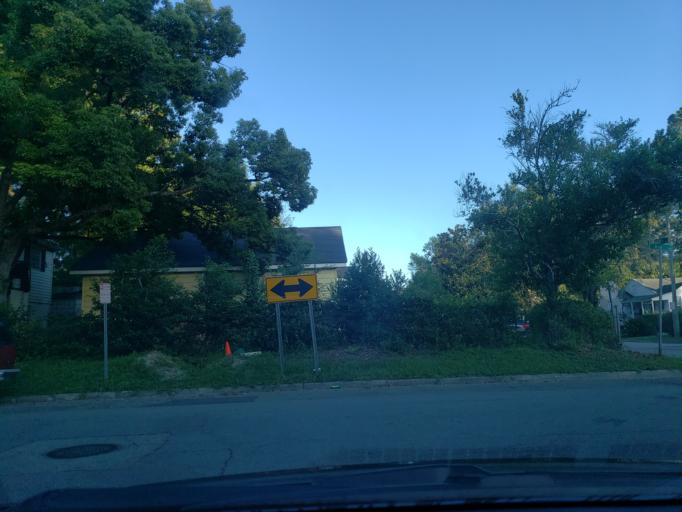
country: US
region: Georgia
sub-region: Chatham County
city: Thunderbolt
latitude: 32.0526
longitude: -81.0778
